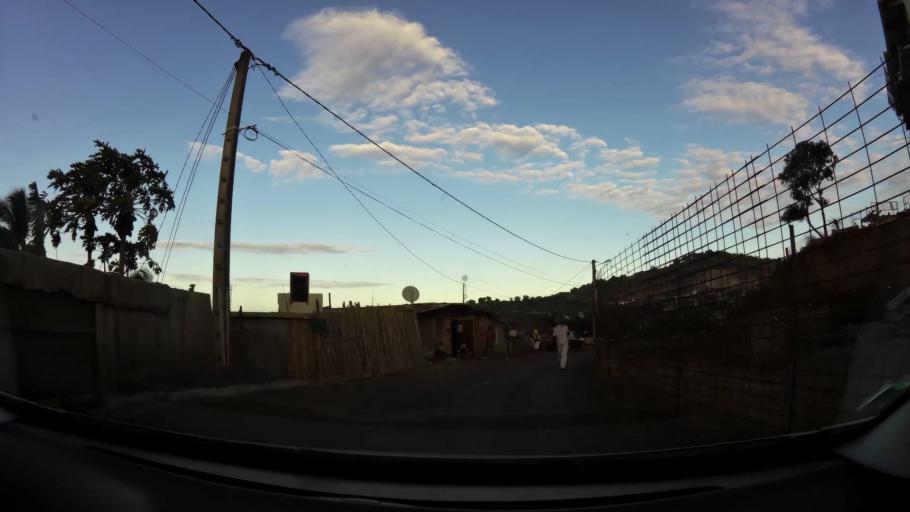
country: YT
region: Koungou
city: Koungou
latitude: -12.7348
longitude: 45.2038
